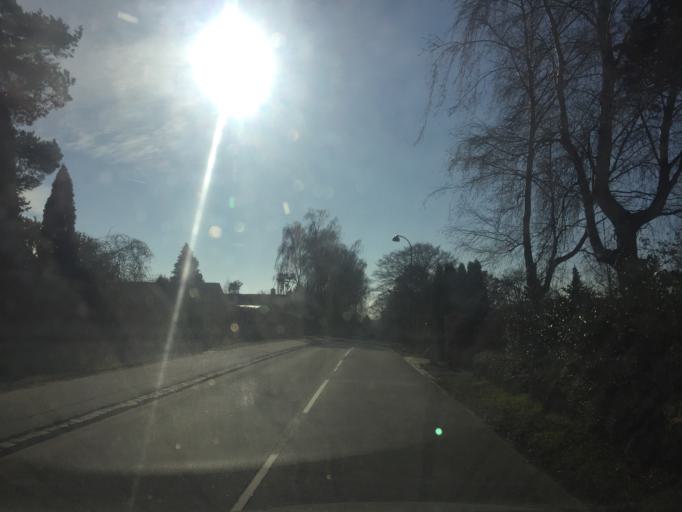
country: DK
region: Capital Region
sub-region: Rudersdal Kommune
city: Trorod
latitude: 55.8581
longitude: 12.5420
